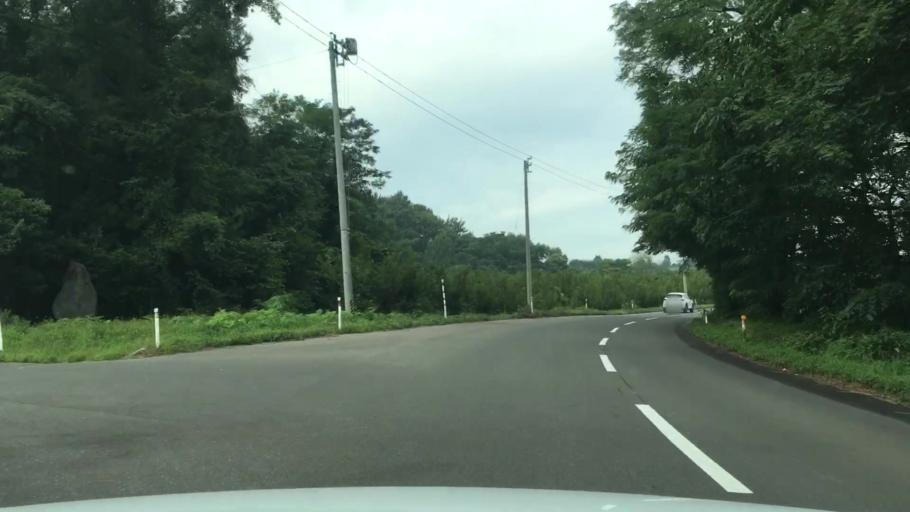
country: JP
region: Aomori
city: Hirosaki
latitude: 40.6689
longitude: 140.3899
